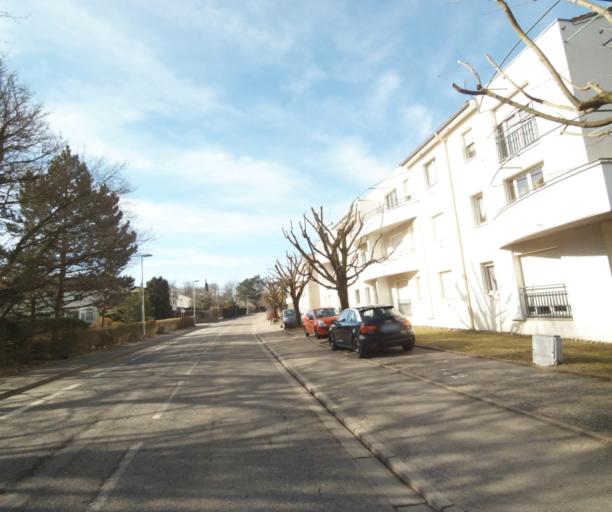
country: FR
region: Lorraine
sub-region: Departement de Meurthe-et-Moselle
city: Villers-les-Nancy
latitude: 48.6501
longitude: 6.1584
